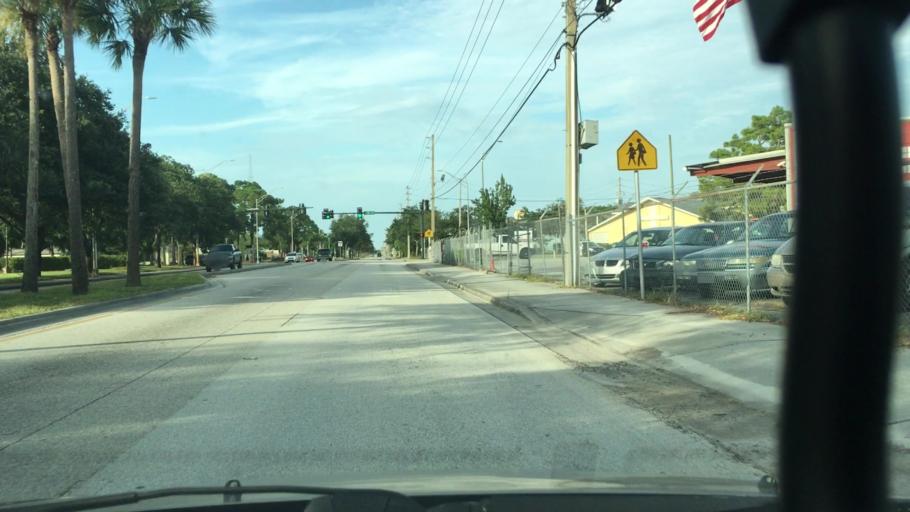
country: US
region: Florida
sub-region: Saint Lucie County
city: Fort Pierce South
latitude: 27.4306
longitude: -80.3592
